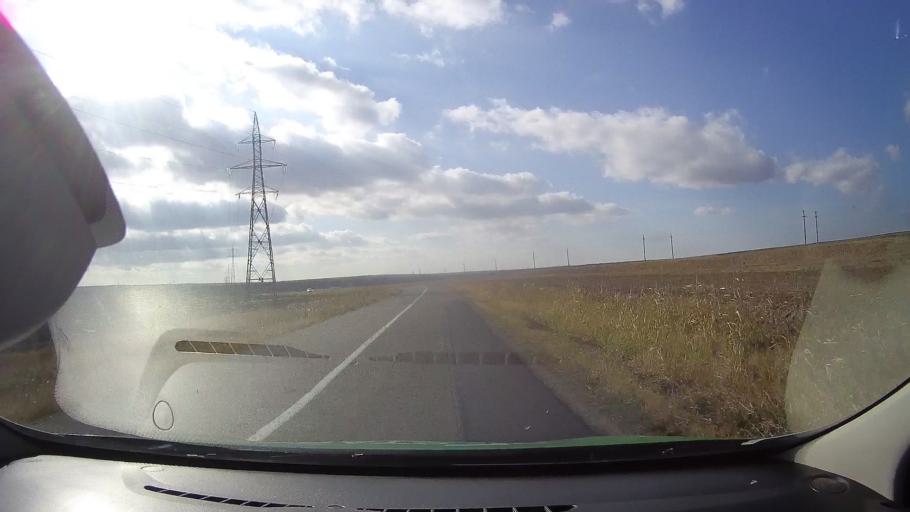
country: RO
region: Constanta
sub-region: Comuna Sacele
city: Sacele
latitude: 44.5037
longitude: 28.6643
